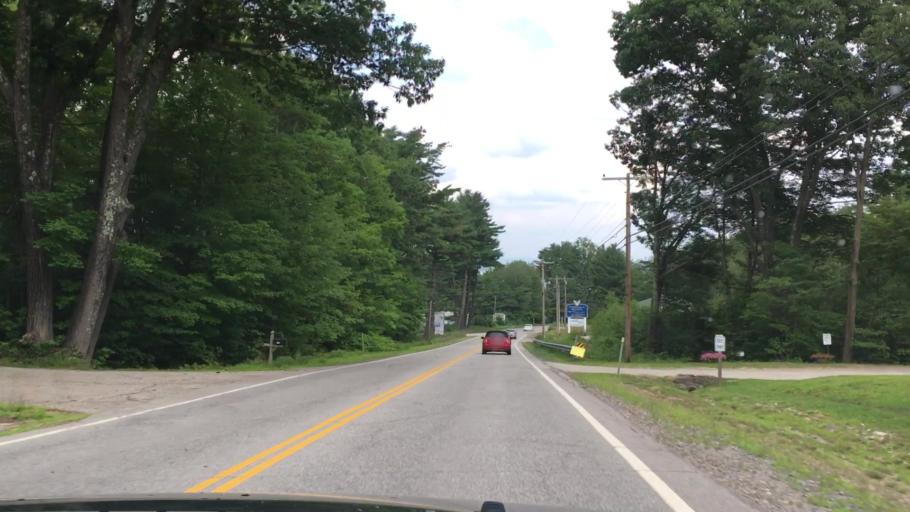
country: US
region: New Hampshire
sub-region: Belknap County
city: Meredith
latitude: 43.6375
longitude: -71.4940
